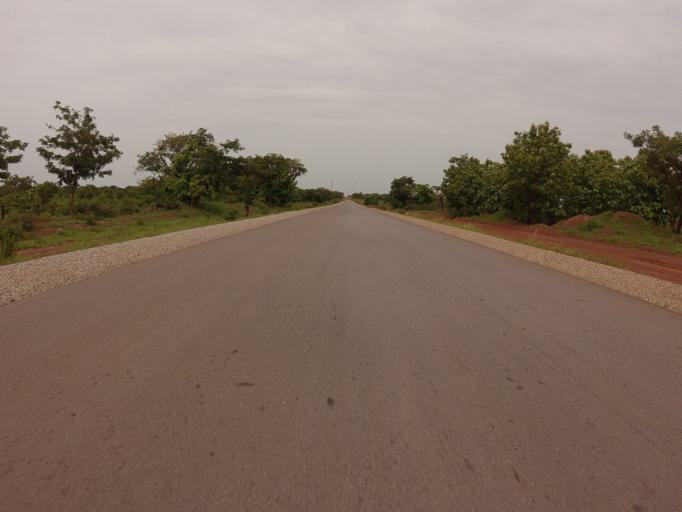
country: GH
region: Northern
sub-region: Yendi
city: Yendi
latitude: 9.1219
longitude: 0.0039
